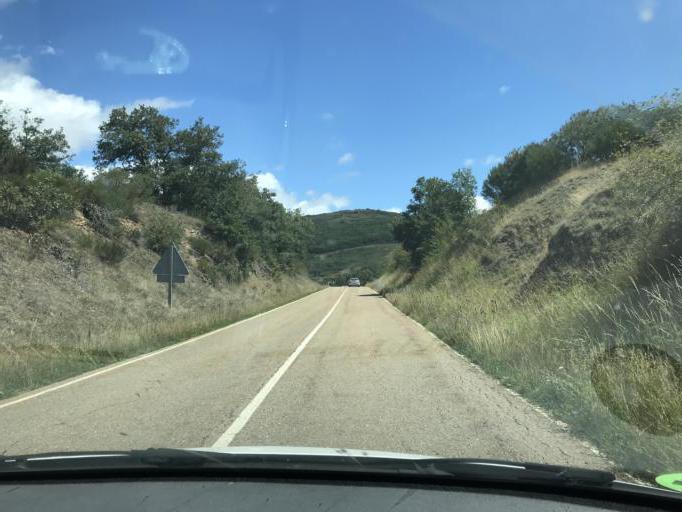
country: ES
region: Castille and Leon
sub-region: Provincia de Palencia
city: Cervera de Pisuerga
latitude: 42.9082
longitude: -4.4919
